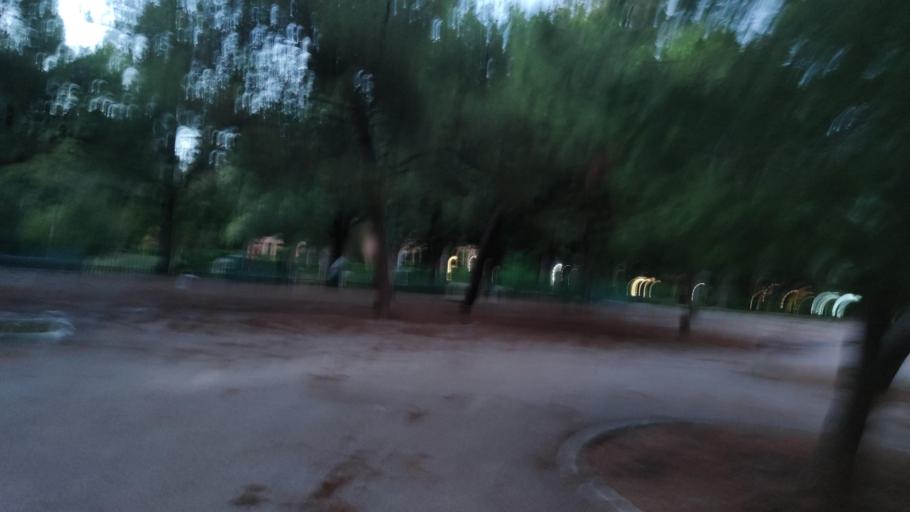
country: IT
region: Sicily
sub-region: Palermo
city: Palermo
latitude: 38.1330
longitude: 13.3518
